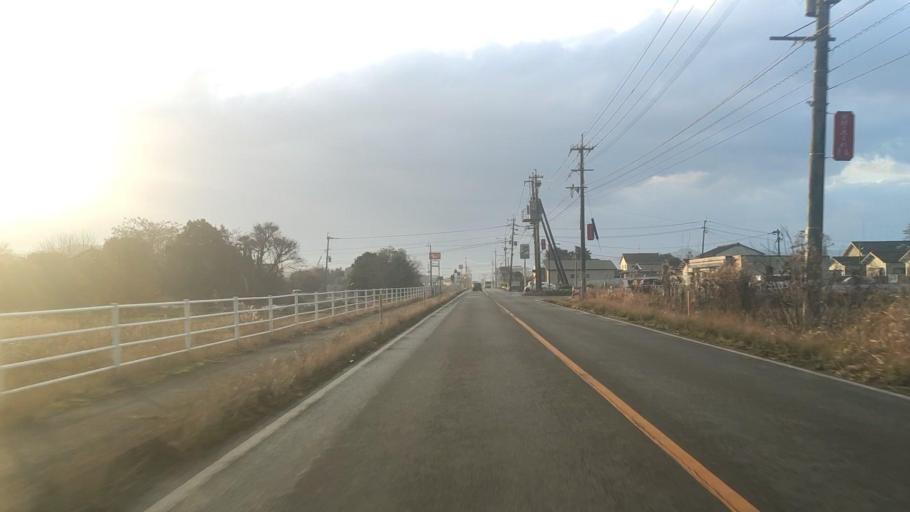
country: JP
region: Kumamoto
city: Uto
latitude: 32.7172
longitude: 130.7721
